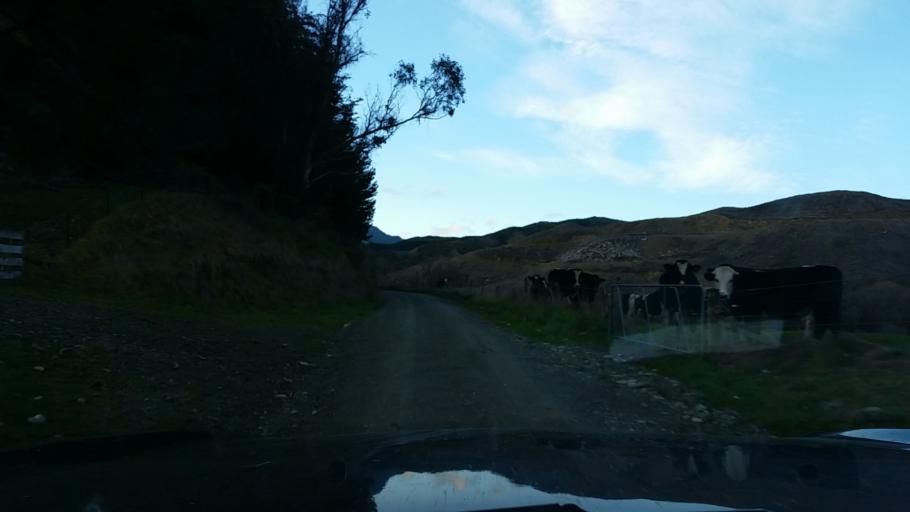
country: NZ
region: Marlborough
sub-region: Marlborough District
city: Blenheim
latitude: -41.5079
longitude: 173.5917
